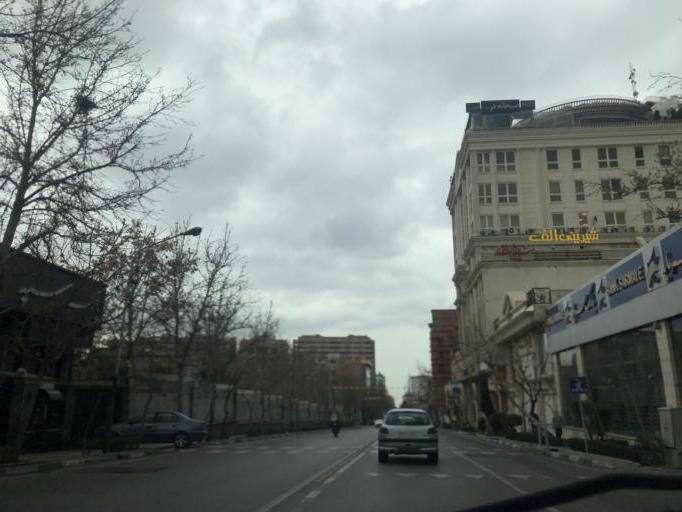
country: IR
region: Tehran
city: Tajrish
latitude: 35.7774
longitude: 51.4660
